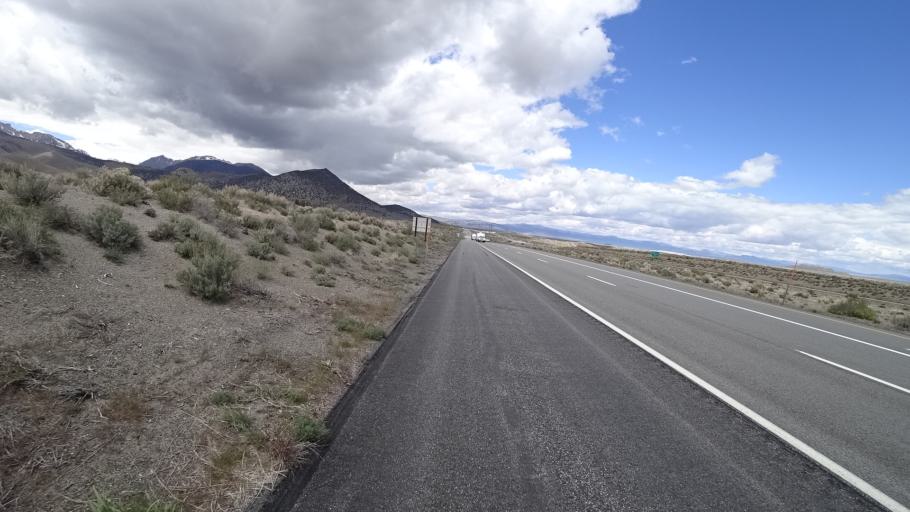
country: US
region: California
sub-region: Mono County
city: Mammoth Lakes
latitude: 37.8876
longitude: -119.0916
